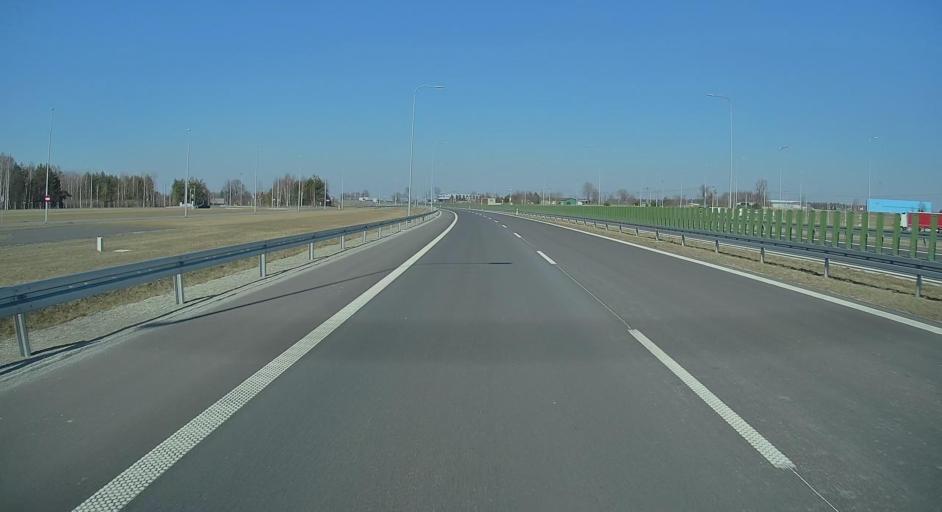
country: PL
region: Lublin Voivodeship
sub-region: Powiat janowski
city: Janow Lubelski
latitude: 50.7173
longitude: 22.3828
